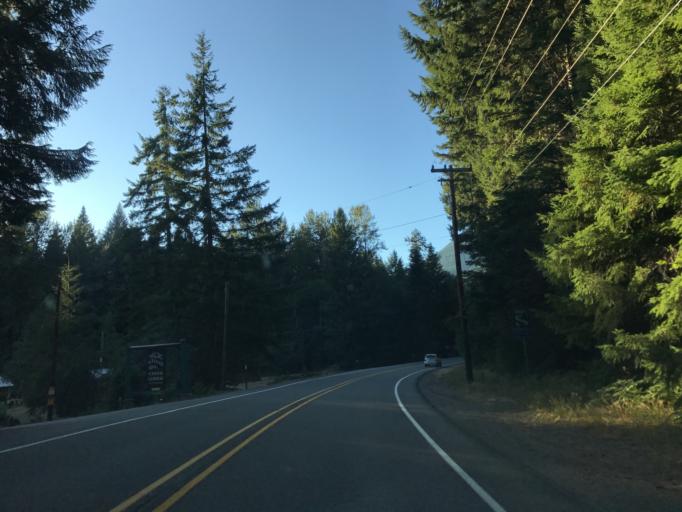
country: US
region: Washington
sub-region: Pierce County
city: Eatonville
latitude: 46.7429
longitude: -121.9224
